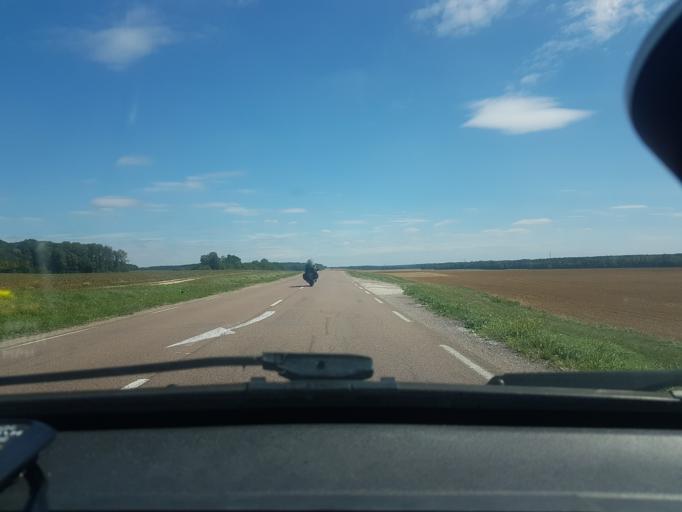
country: FR
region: Bourgogne
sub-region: Departement de la Cote-d'Or
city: Pontailler-sur-Saone
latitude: 47.3999
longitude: 5.4200
